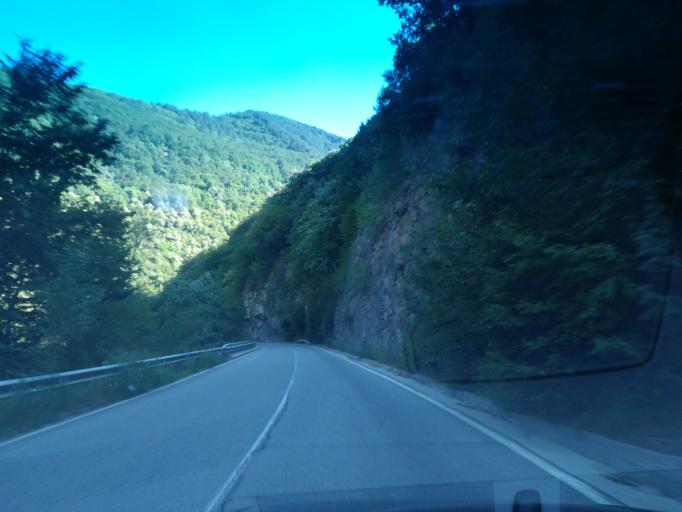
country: BG
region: Plovdiv
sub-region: Obshtina Luki
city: Luki
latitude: 41.9229
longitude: 24.8268
